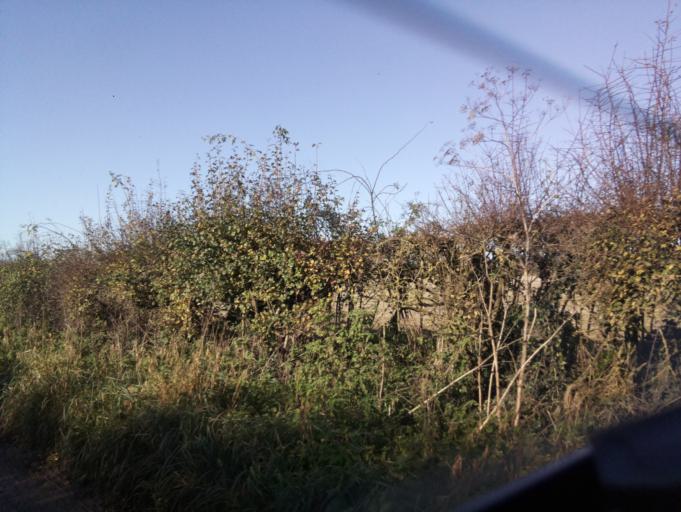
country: GB
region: England
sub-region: Somerset
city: Langport
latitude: 51.0357
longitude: -2.8004
